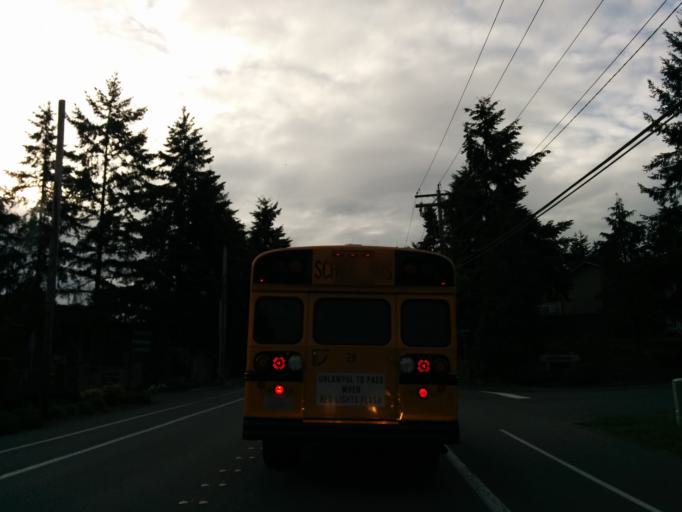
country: US
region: Washington
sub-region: King County
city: Redmond
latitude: 47.6498
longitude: -122.1126
